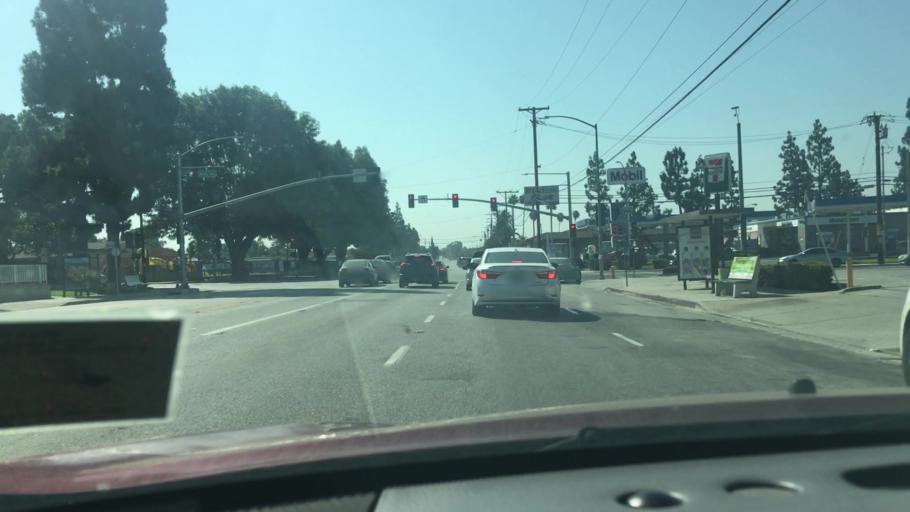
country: US
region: California
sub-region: Los Angeles County
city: South Whittier
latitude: 33.9433
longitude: -118.0282
